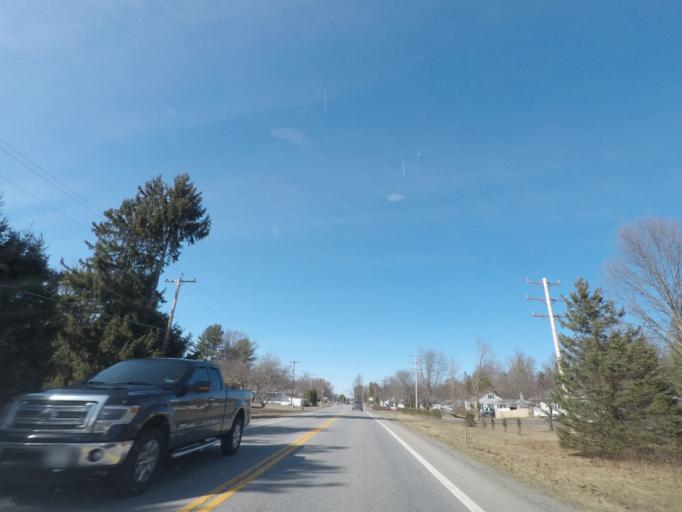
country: US
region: New York
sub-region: Saratoga County
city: Milton
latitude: 43.0391
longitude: -73.8495
